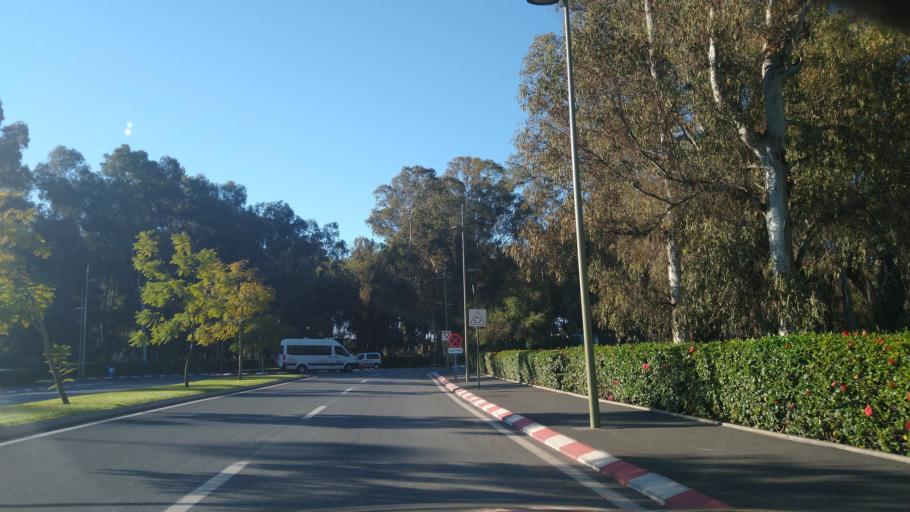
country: MA
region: Rabat-Sale-Zemmour-Zaer
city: Sale
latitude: 34.0345
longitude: -6.7497
